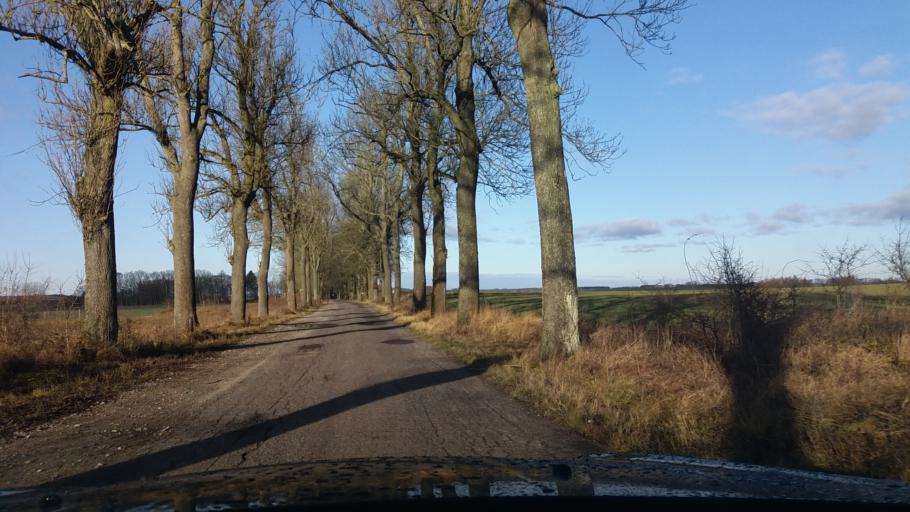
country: PL
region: West Pomeranian Voivodeship
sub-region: Powiat choszczenski
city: Drawno
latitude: 53.1875
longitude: 15.7951
